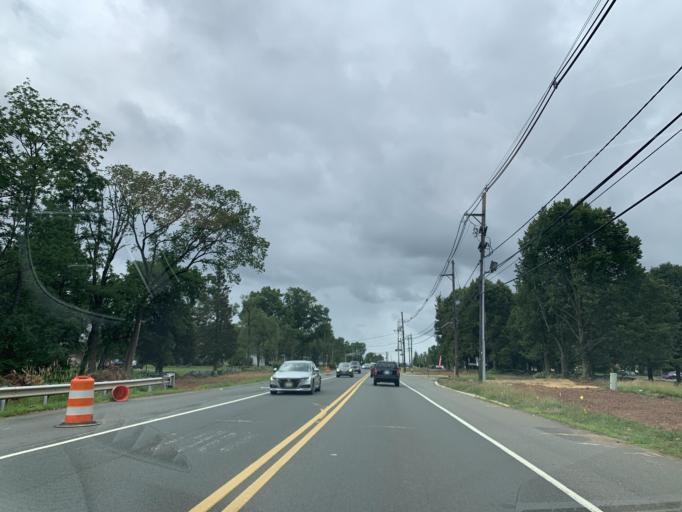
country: US
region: New Jersey
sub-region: Somerset County
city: Bloomingdale
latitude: 40.5257
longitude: -74.6274
